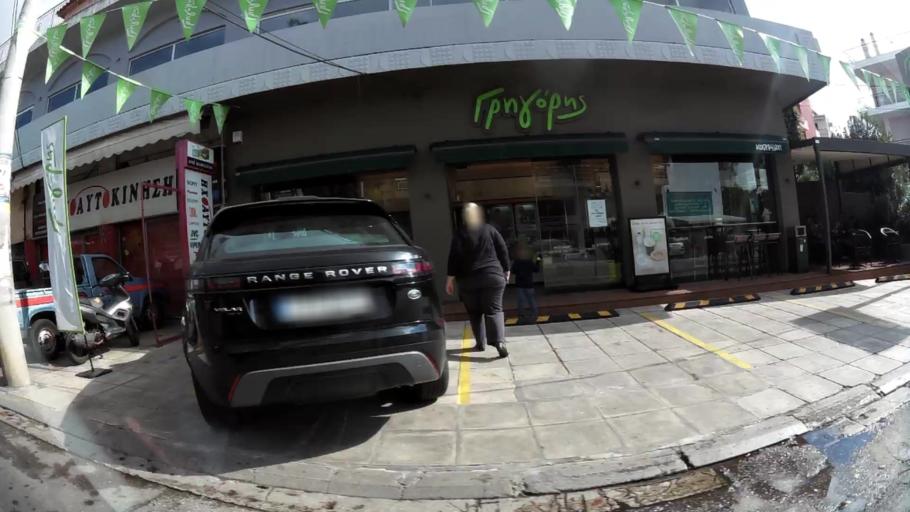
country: GR
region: Attica
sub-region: Nomarchia Athinas
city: Melissia
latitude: 38.0580
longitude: 23.8383
